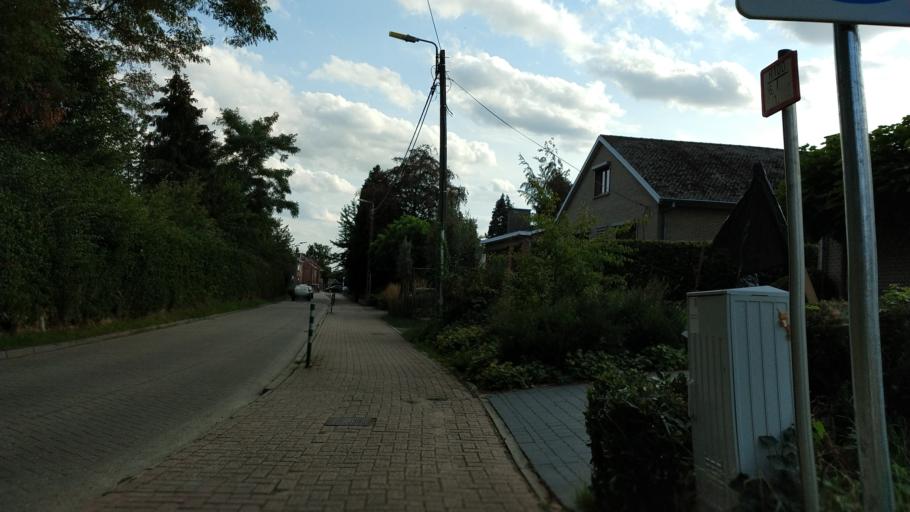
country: BE
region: Flanders
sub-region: Provincie Vlaams-Brabant
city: Bierbeek
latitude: 50.8671
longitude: 4.7629
